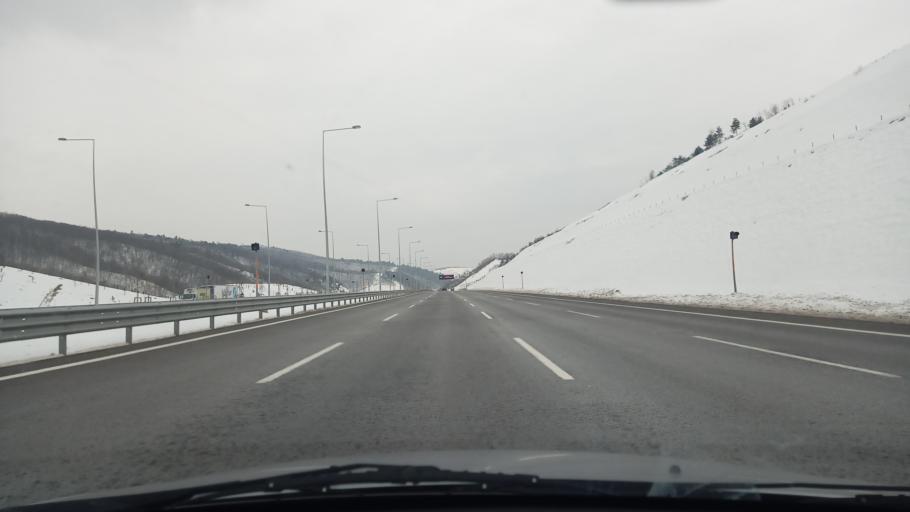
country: TR
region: Kocaeli
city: Izmit
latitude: 40.8525
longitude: 29.8925
